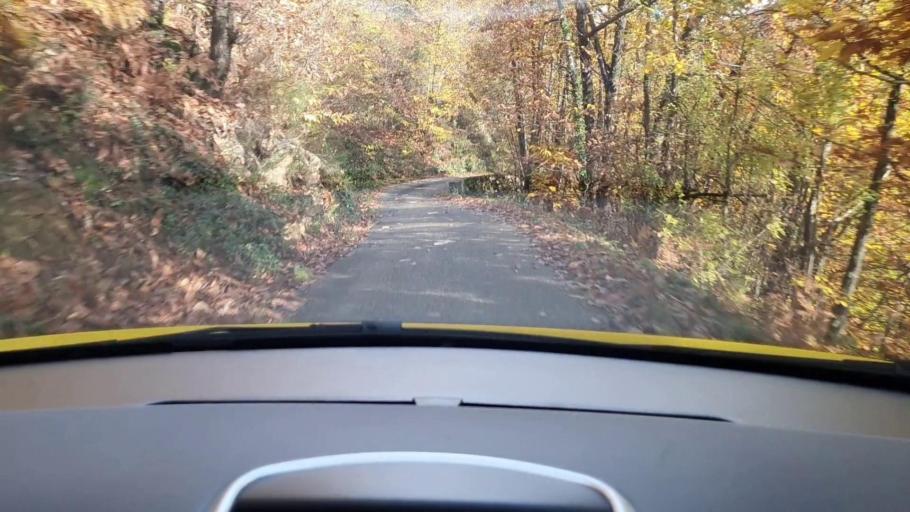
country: FR
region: Languedoc-Roussillon
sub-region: Departement du Gard
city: Valleraugue
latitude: 44.0918
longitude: 3.7412
